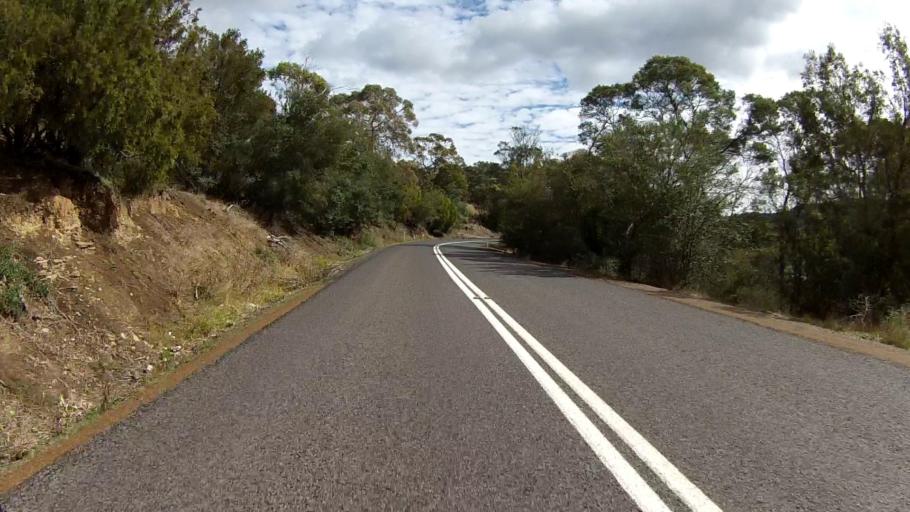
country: AU
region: Tasmania
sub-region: Clarence
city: Lindisfarne
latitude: -42.8058
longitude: 147.3543
